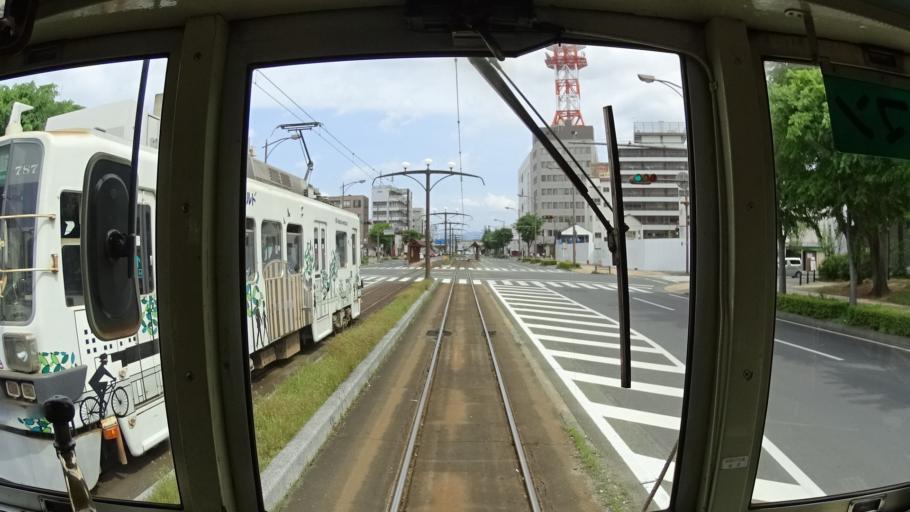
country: JP
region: Aichi
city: Toyohashi
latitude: 34.7652
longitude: 137.3903
